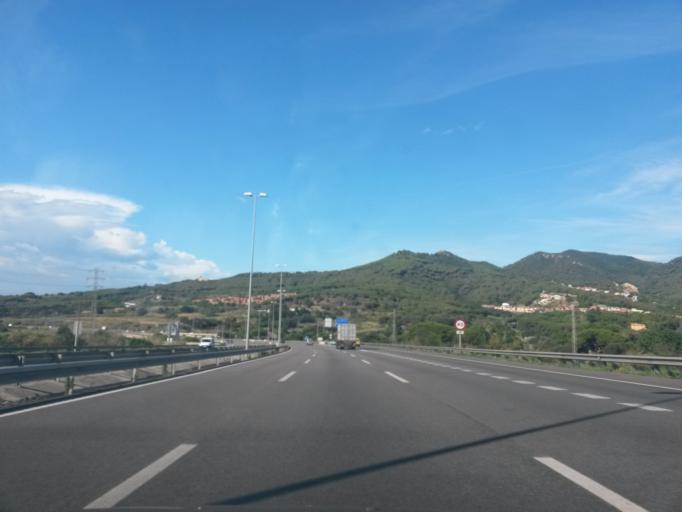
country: ES
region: Catalonia
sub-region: Provincia de Barcelona
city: Argentona
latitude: 41.5480
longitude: 2.4181
